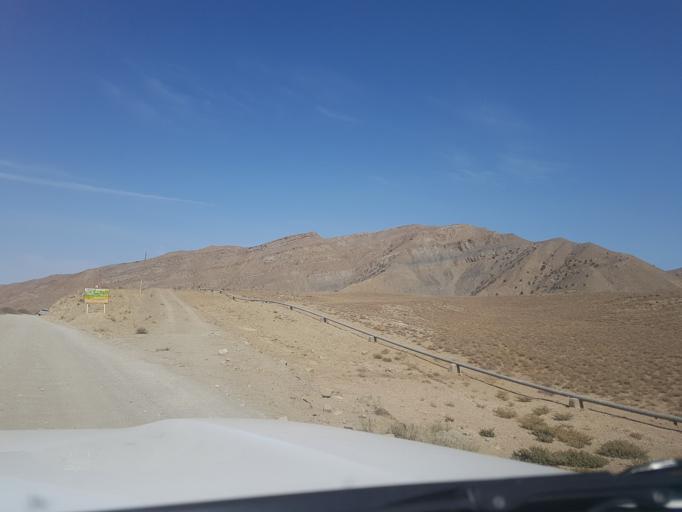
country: TM
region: Ahal
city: Baharly
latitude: 38.4435
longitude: 57.0428
